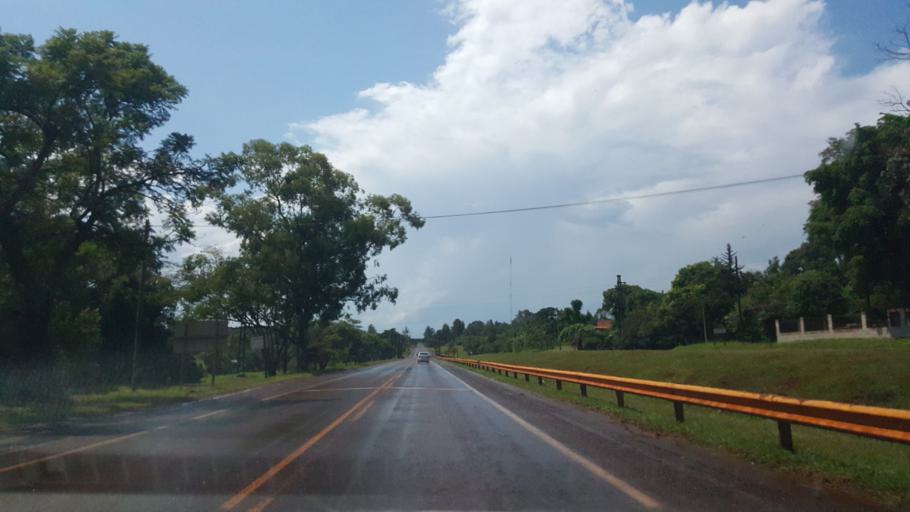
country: AR
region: Misiones
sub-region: Departamento de Eldorado
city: Eldorado
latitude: -26.3977
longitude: -54.6330
